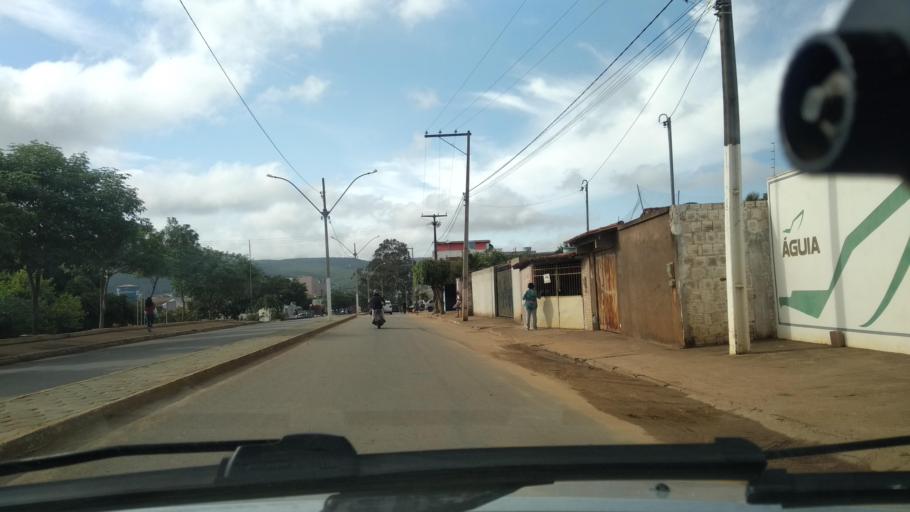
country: BR
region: Bahia
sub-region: Caetite
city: Caetite
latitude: -14.0578
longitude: -42.4839
